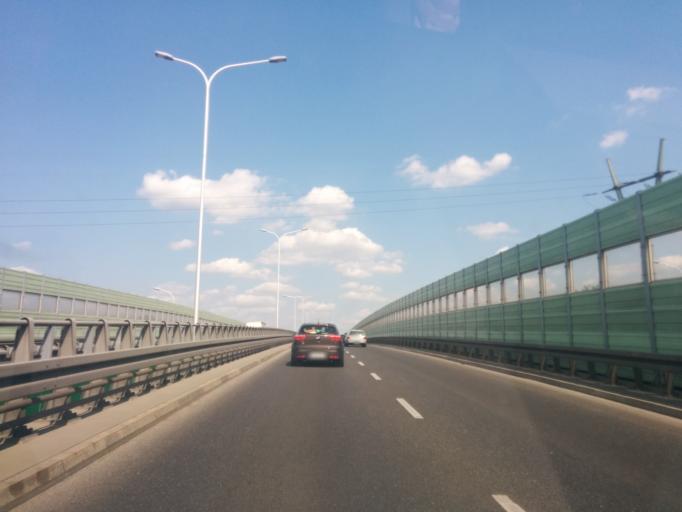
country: PL
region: Masovian Voivodeship
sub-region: Warszawa
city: Bialoleka
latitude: 52.3153
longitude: 20.9765
